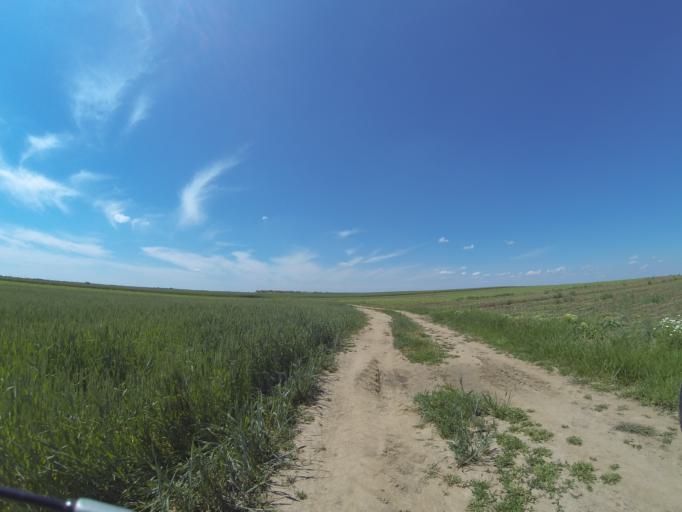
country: RO
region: Dolj
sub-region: Comuna Leu
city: Leu
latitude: 44.2186
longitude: 24.0135
